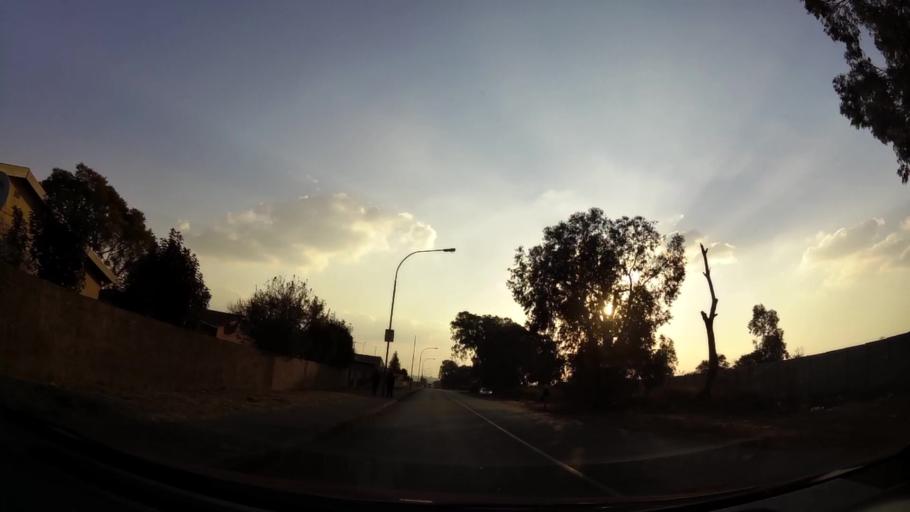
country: ZA
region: Gauteng
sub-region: City of Johannesburg Metropolitan Municipality
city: Soweto
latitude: -26.2806
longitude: 27.9006
